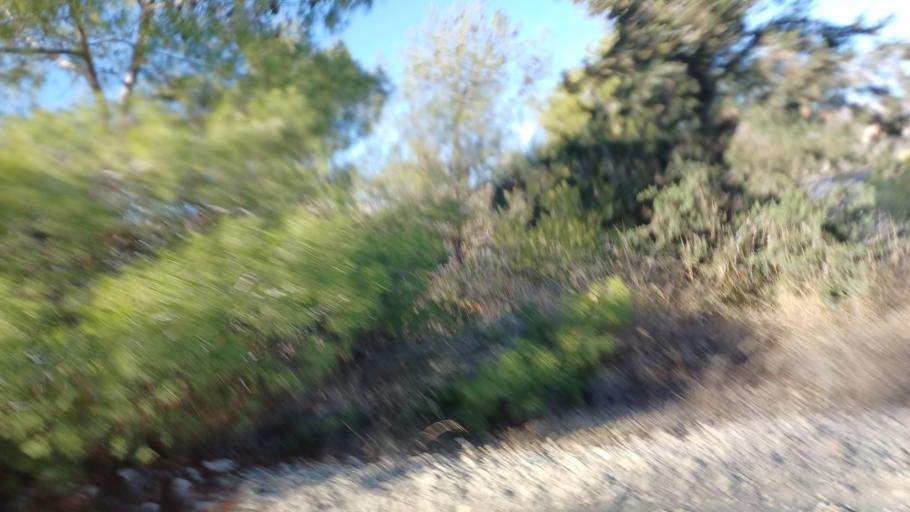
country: CY
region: Larnaka
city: Psevdas
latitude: 34.9622
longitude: 33.5135
